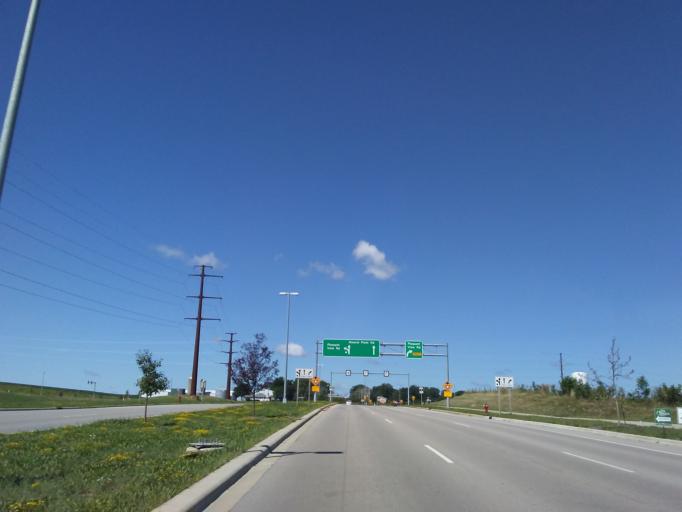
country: US
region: Wisconsin
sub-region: Dane County
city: Middleton
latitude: 43.0604
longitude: -89.5340
